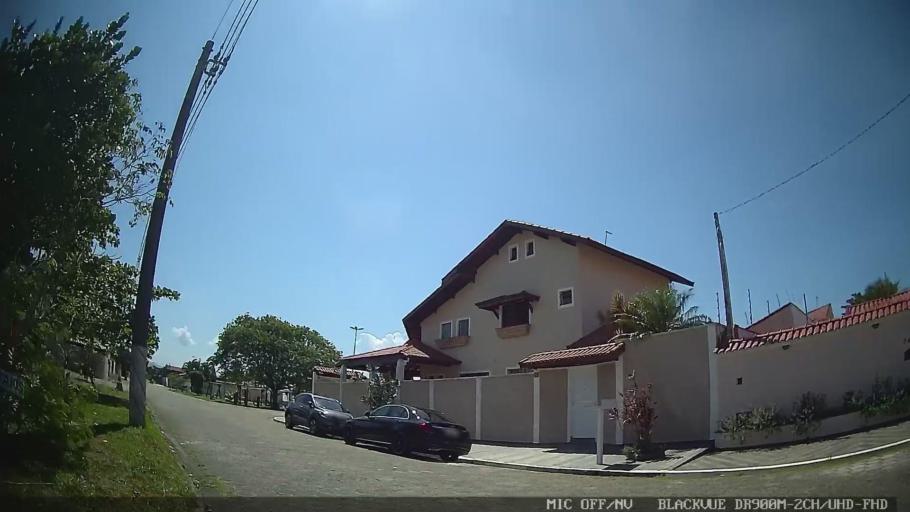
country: BR
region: Sao Paulo
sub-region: Peruibe
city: Peruibe
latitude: -24.3016
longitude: -46.9803
